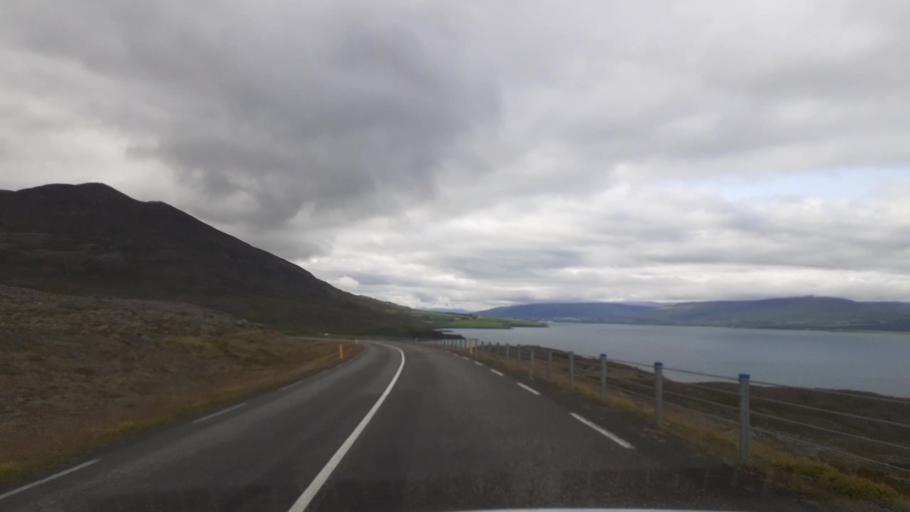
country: IS
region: Northeast
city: Akureyri
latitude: 65.8291
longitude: -18.0583
